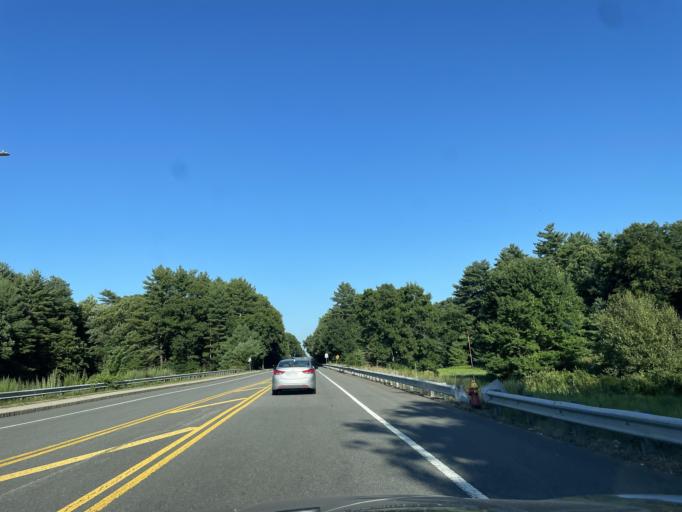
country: US
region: Massachusetts
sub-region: Bristol County
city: Mansfield Center
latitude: 42.0285
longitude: -71.1796
